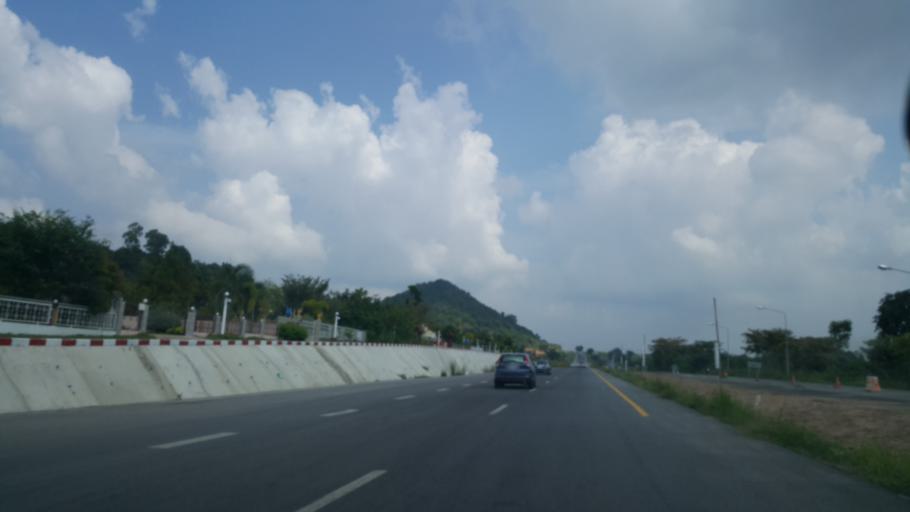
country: TH
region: Rayong
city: Ban Chang
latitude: 12.7445
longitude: 100.9908
